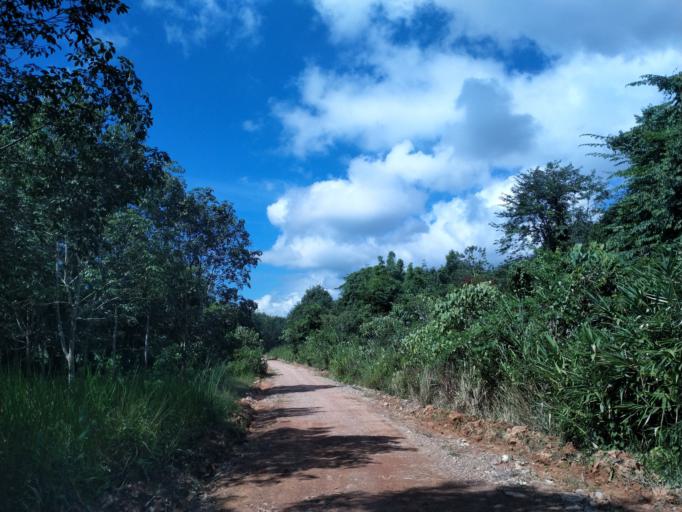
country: TH
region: Nong Khai
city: Rattanawapi
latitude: 18.6376
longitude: 102.9348
